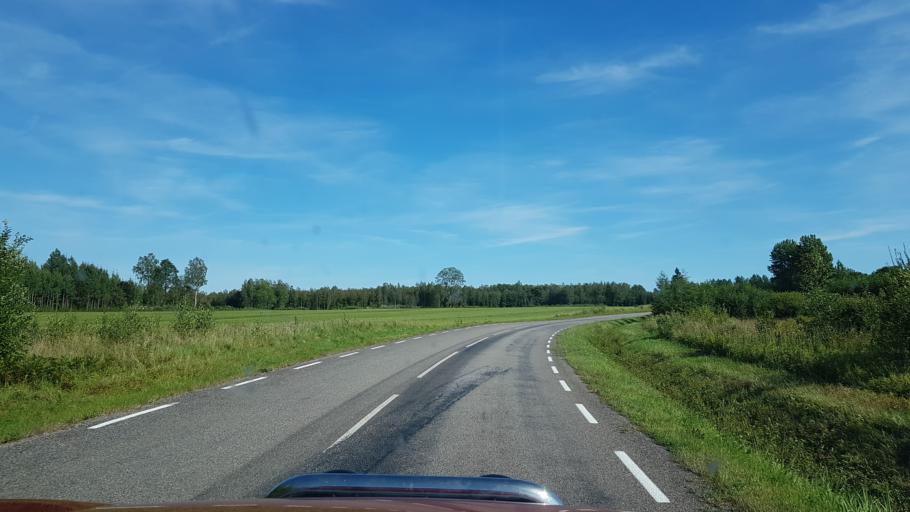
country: EE
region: Paernumaa
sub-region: Saarde vald
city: Kilingi-Nomme
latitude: 58.1277
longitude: 25.0062
